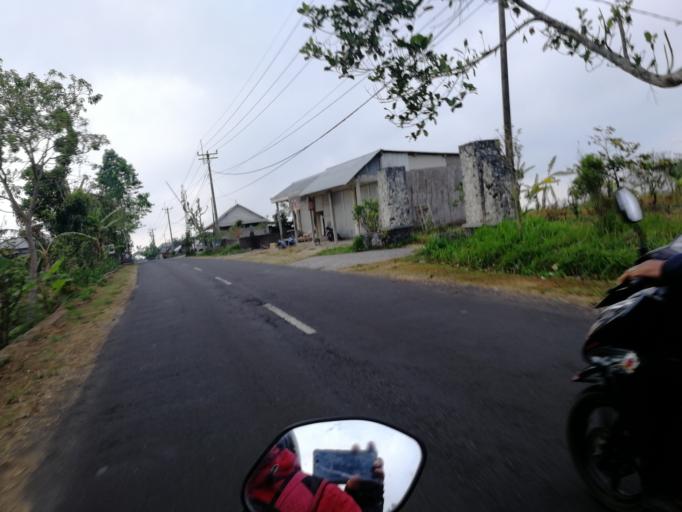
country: ID
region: Bali
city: Banjar Kedisan
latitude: -8.2430
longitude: 115.2438
